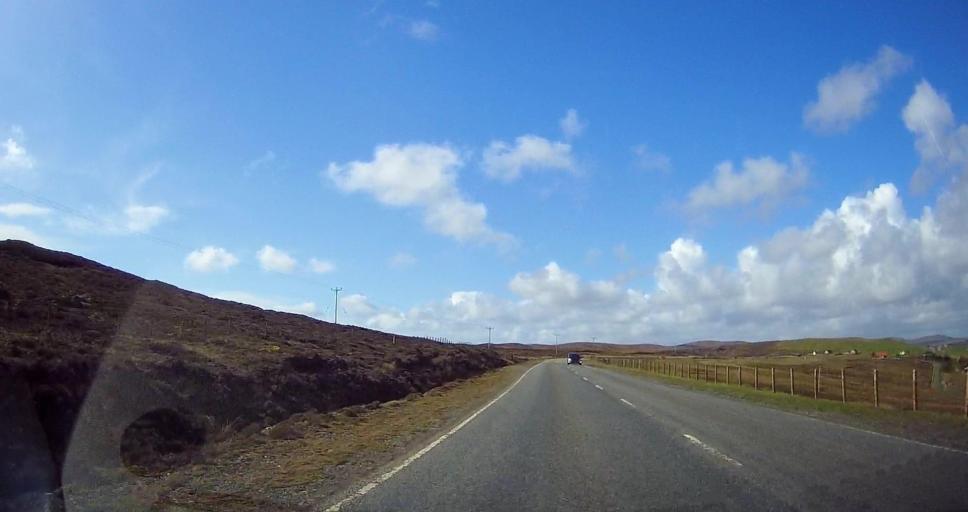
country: GB
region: Scotland
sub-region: Shetland Islands
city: Lerwick
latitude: 60.2268
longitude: -1.2359
